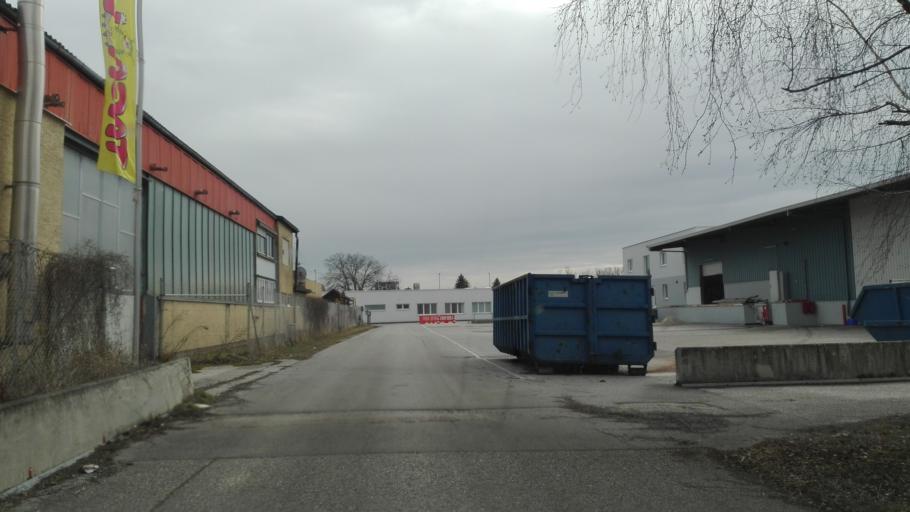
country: AT
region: Upper Austria
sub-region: Politischer Bezirk Linz-Land
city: Traun
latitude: 48.2321
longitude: 14.2185
